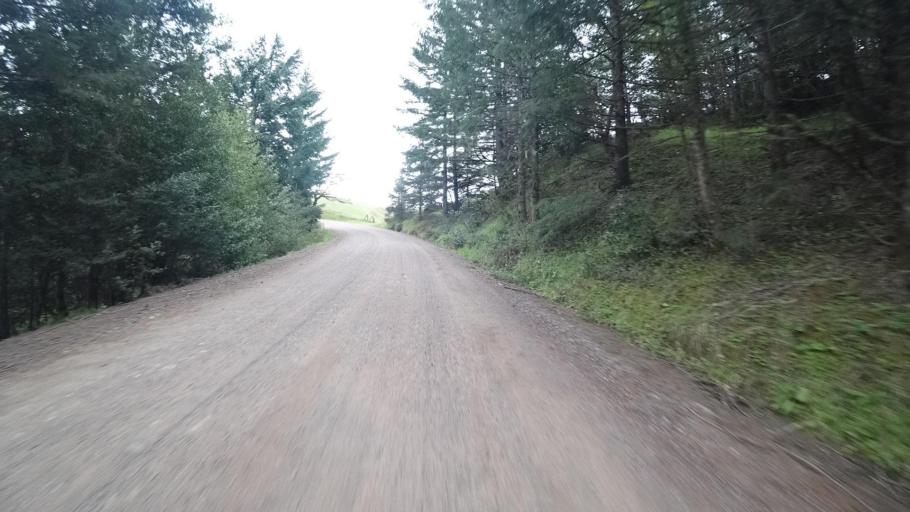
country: US
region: California
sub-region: Humboldt County
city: Redway
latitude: 40.2132
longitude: -123.7441
